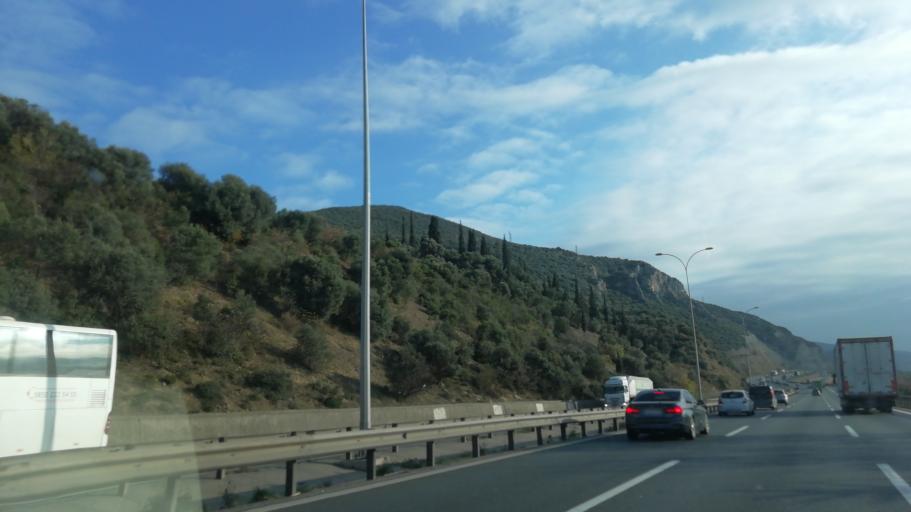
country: TR
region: Kocaeli
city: Hereke
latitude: 40.7773
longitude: 29.6402
